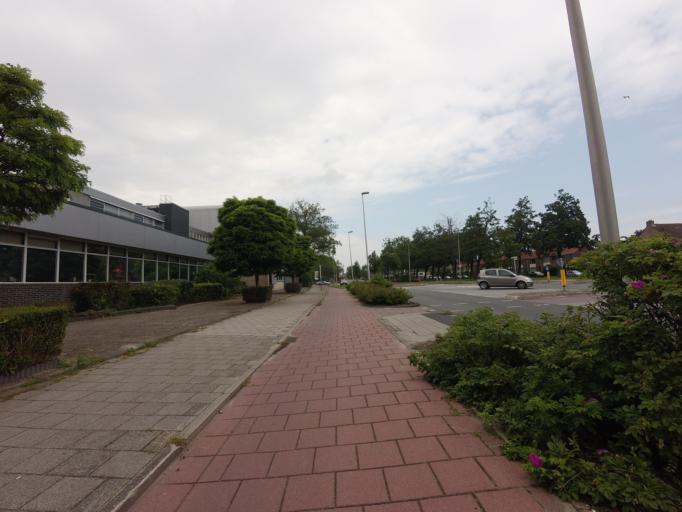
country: NL
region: North Holland
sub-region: Gemeente Purmerend
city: Purmerend
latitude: 52.5091
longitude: 4.9675
